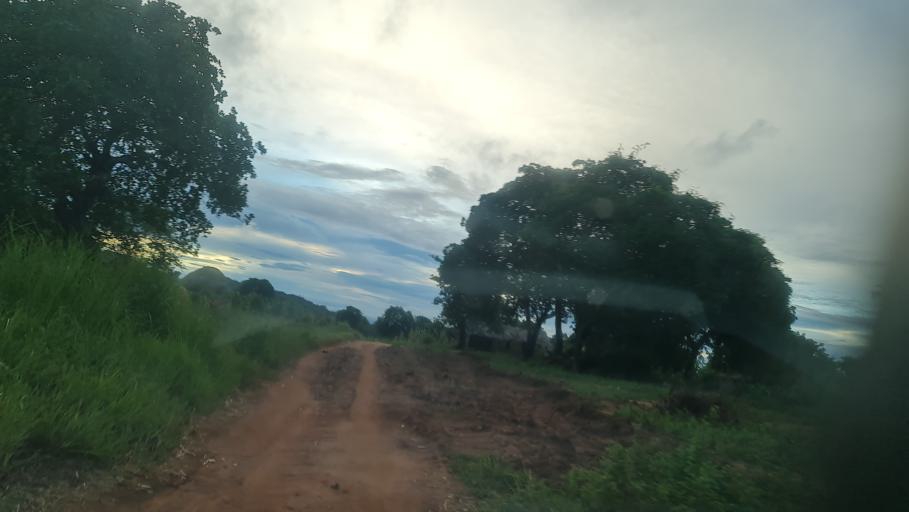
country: MZ
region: Nampula
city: Nampula
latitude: -14.7408
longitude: 39.9368
